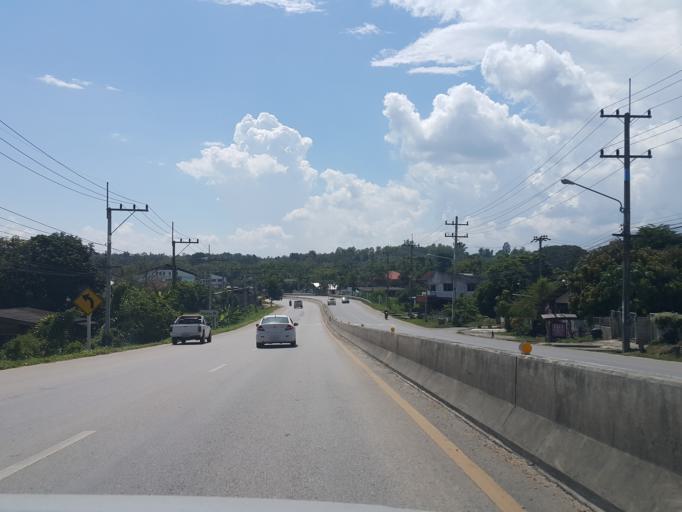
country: TH
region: Chiang Mai
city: Mae Taeng
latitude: 19.0584
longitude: 98.9425
